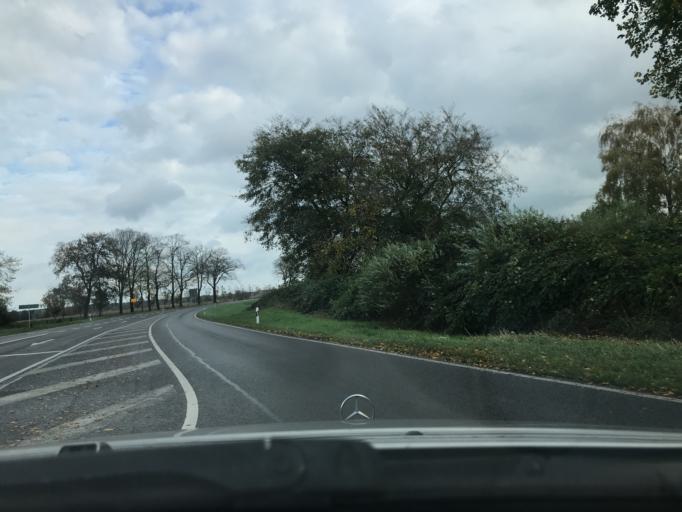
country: DE
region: Mecklenburg-Vorpommern
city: Karlshagen
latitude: 54.0702
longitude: 13.8608
